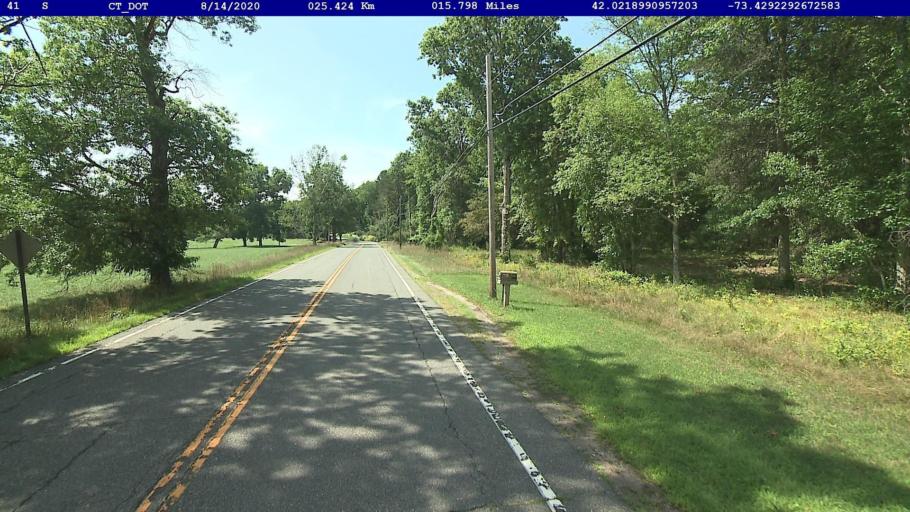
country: US
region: Connecticut
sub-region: Litchfield County
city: Canaan
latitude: 42.0219
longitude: -73.4292
